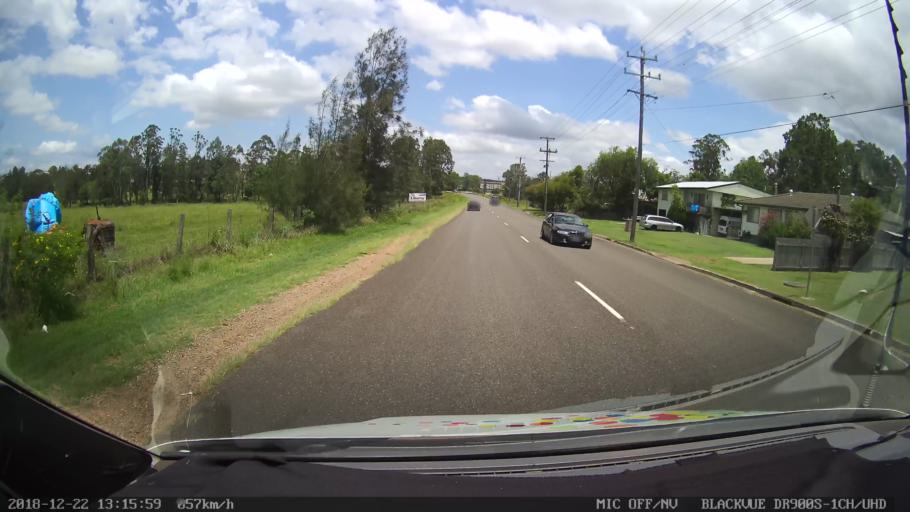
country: AU
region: New South Wales
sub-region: Clarence Valley
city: South Grafton
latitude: -29.7223
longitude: 152.9384
